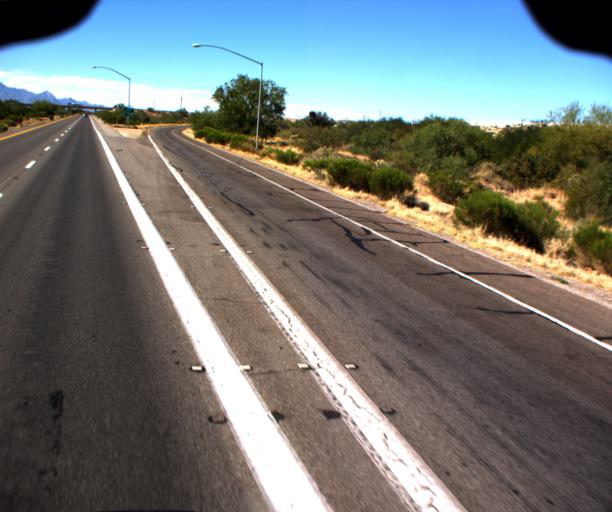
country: US
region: Arizona
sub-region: Pima County
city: Sahuarita
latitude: 31.9626
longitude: -110.9885
